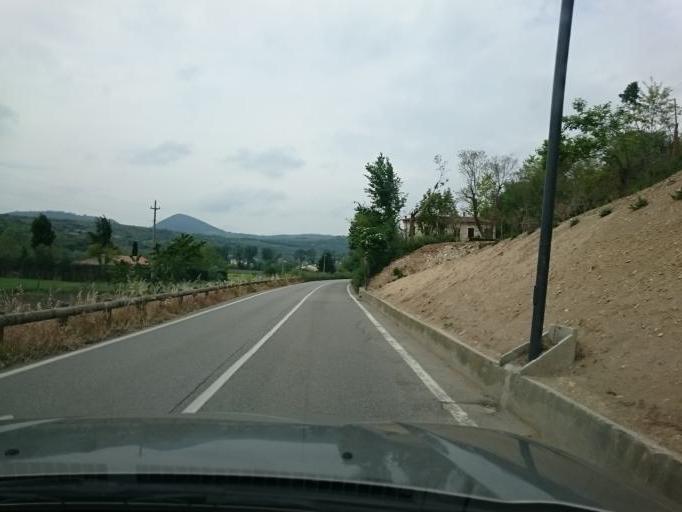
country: IT
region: Veneto
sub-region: Provincia di Padova
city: Arqua Petrarca
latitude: 45.2573
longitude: 11.7136
